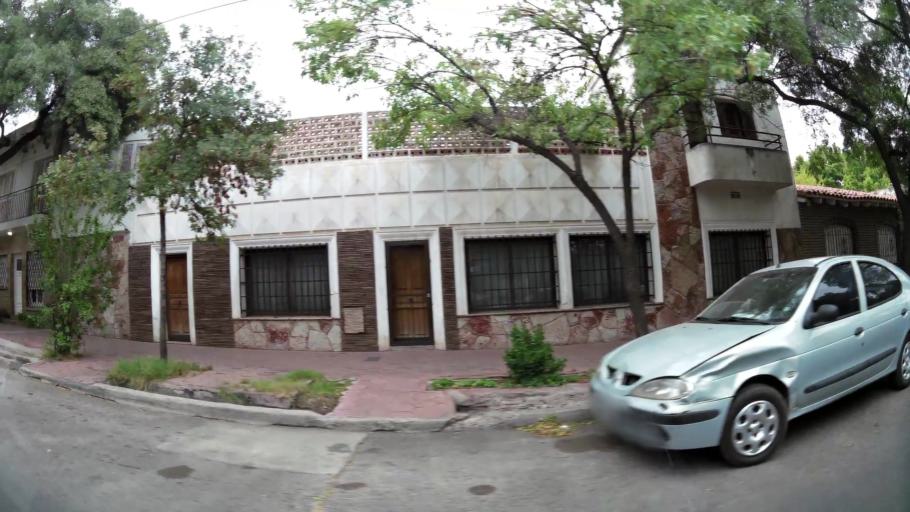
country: AR
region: Mendoza
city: Mendoza
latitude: -32.8770
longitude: -68.8510
